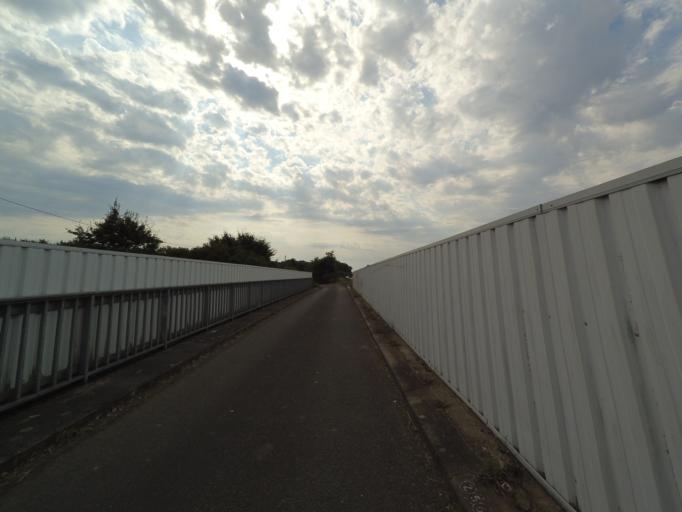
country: FR
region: Pays de la Loire
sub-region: Departement de la Vendee
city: Bouffere
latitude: 46.9734
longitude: -1.3677
